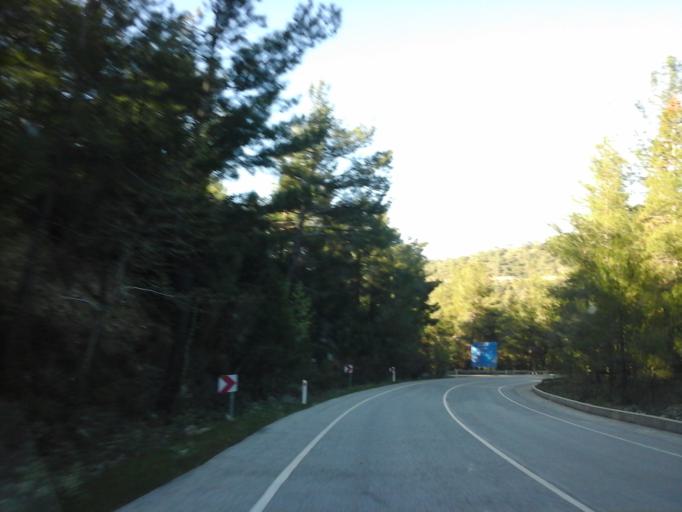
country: CY
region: Lefkosia
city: Kakopetria
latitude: 34.9594
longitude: 32.9223
